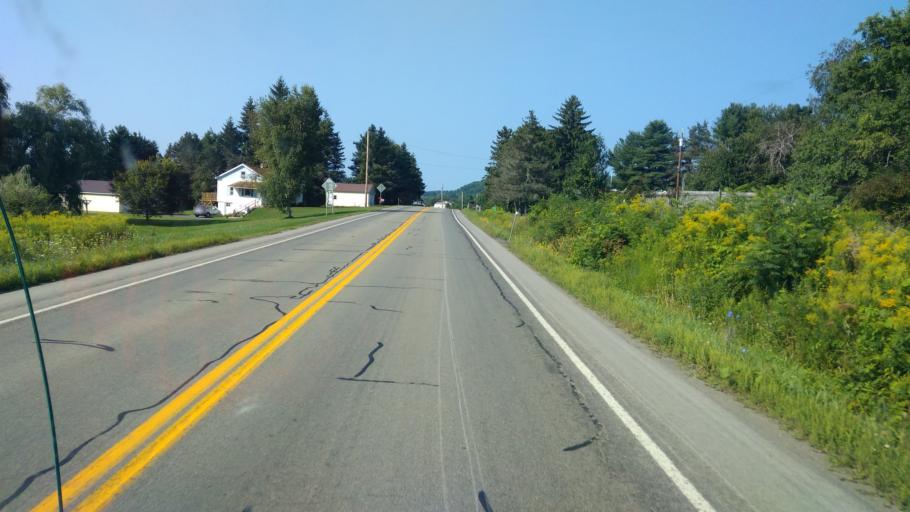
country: US
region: New York
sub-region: Allegany County
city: Friendship
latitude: 42.3039
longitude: -78.1797
